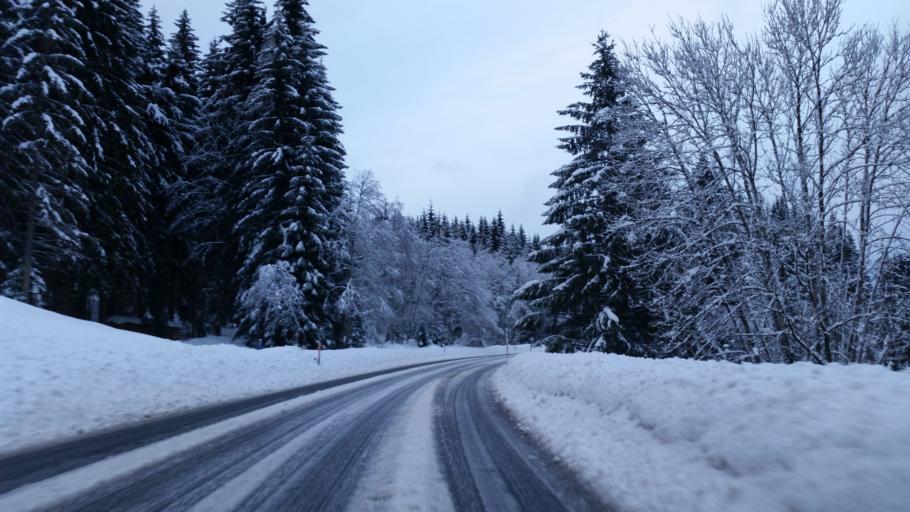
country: AT
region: Tyrol
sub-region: Politischer Bezirk Kitzbuhel
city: Hochfilzen
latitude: 47.4549
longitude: 12.6455
